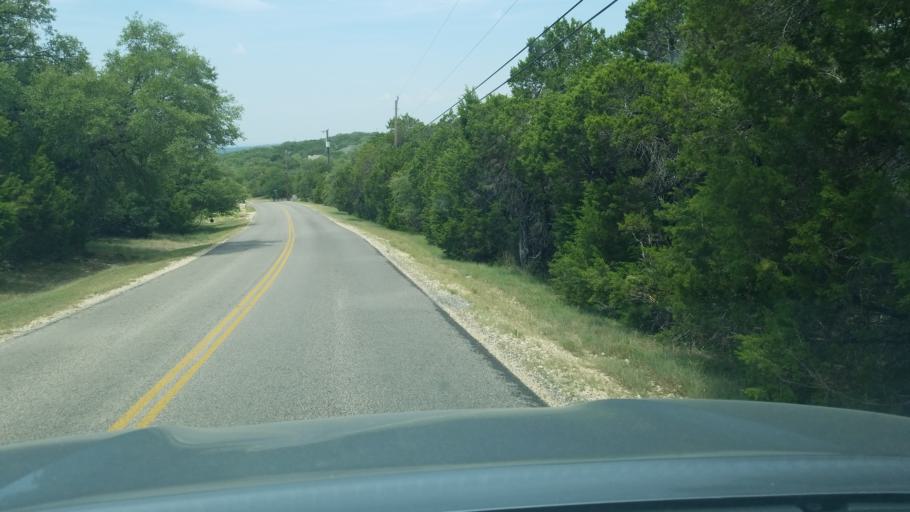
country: US
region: Texas
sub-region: Comal County
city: Bulverde
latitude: 29.7757
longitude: -98.4400
